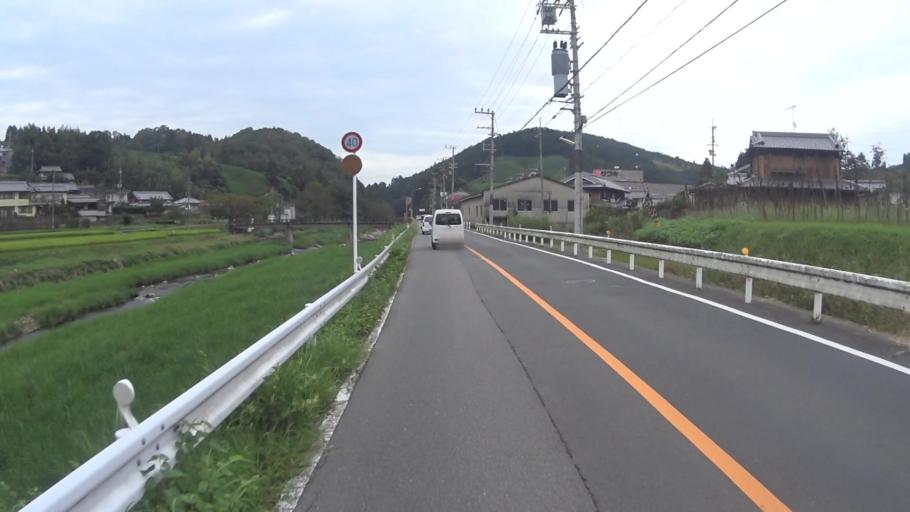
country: JP
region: Kyoto
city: Tanabe
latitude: 34.7896
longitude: 135.8949
